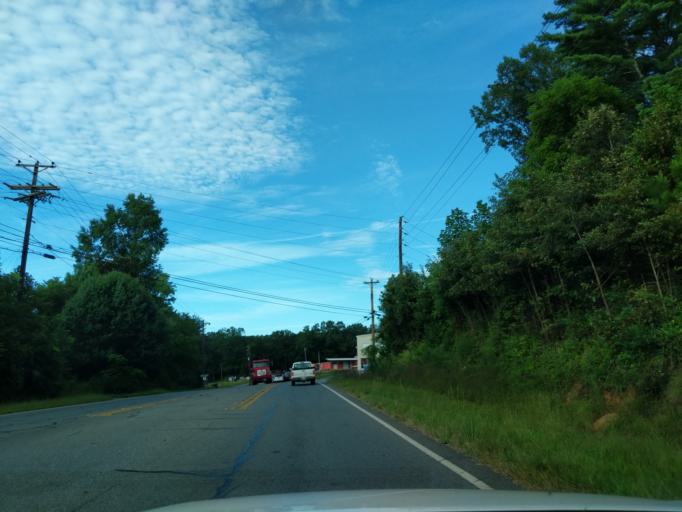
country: US
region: Georgia
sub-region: Fannin County
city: McCaysville
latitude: 34.9466
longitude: -84.3734
